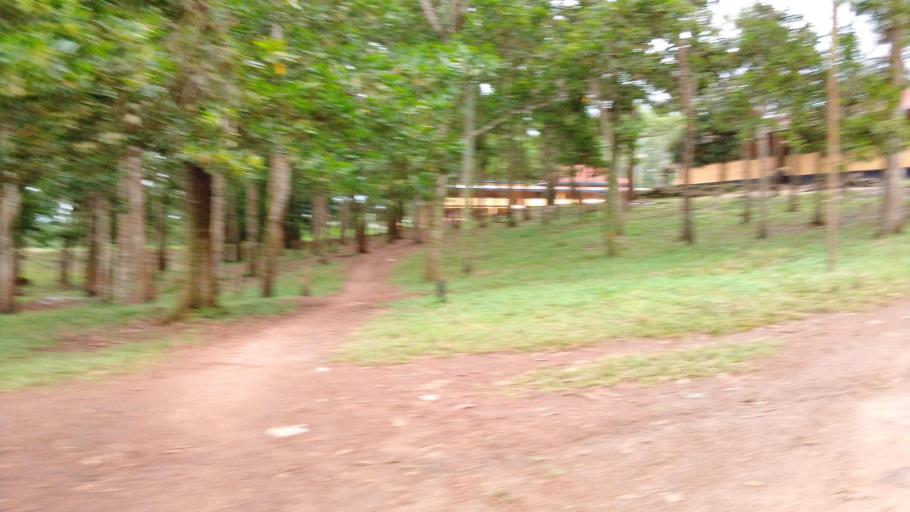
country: SL
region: Eastern Province
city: Kenema
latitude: 7.8809
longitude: -11.1965
